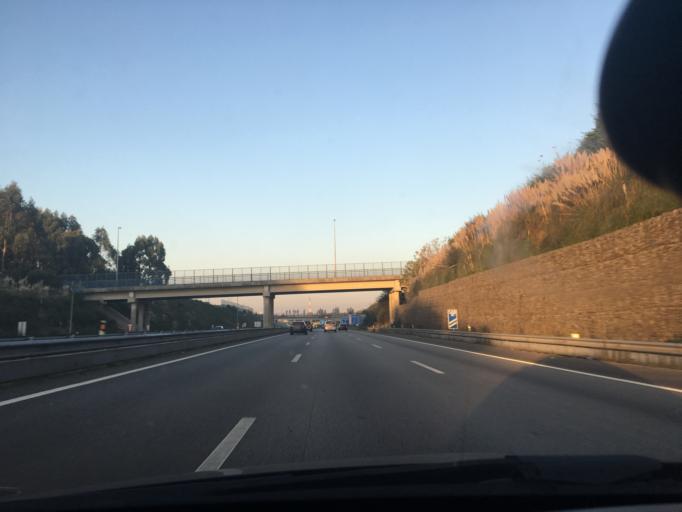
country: PT
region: Porto
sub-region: Matosinhos
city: Guifoes
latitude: 41.1974
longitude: -8.6624
